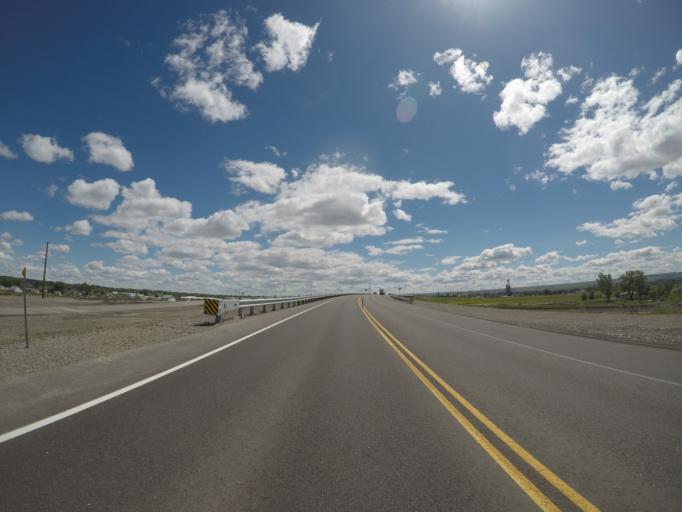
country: US
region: Montana
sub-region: Yellowstone County
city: Laurel
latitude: 45.6640
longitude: -108.7947
